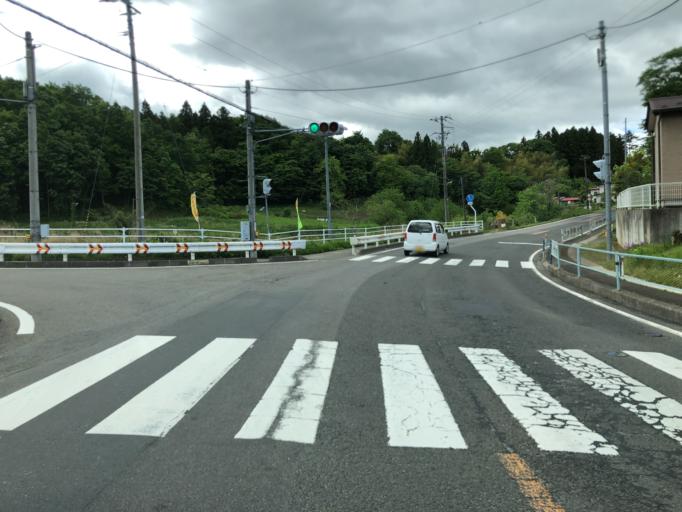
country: JP
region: Fukushima
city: Nihommatsu
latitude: 37.5651
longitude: 140.4566
